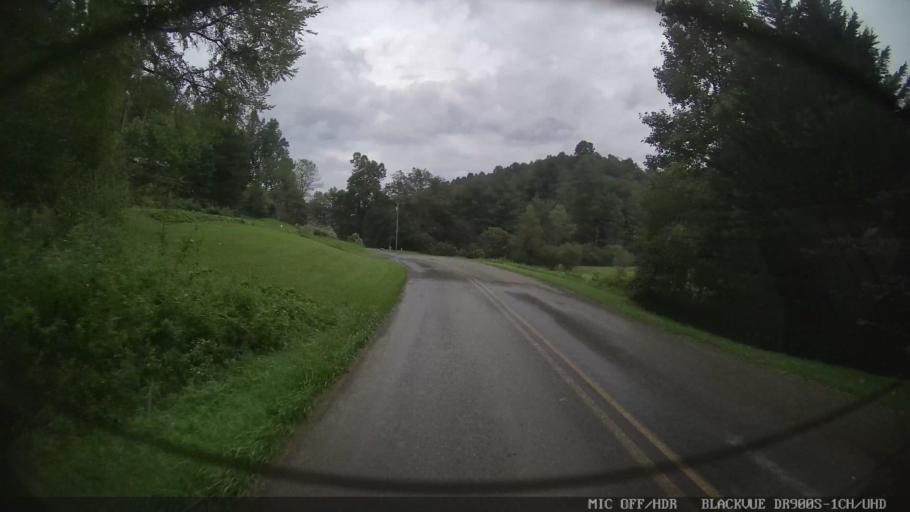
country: US
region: Georgia
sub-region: Gilmer County
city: Ellijay
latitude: 34.7895
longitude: -84.5559
